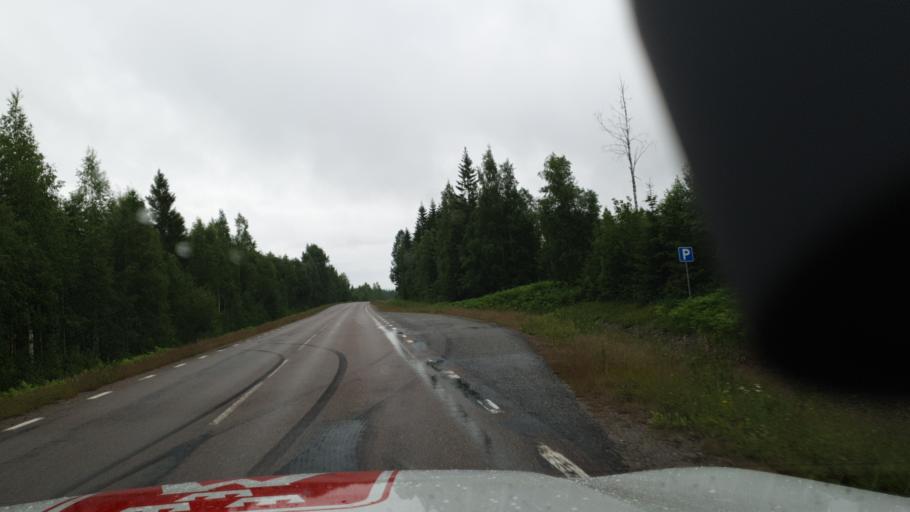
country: SE
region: Vaesterbotten
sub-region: Vannas Kommun
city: Vaennaes
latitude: 63.7936
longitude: 19.8117
